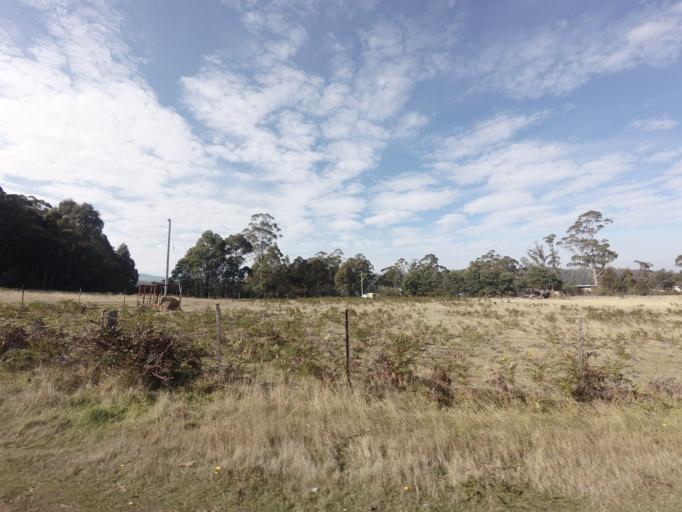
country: AU
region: Tasmania
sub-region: Sorell
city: Sorell
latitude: -42.4993
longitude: 147.4794
